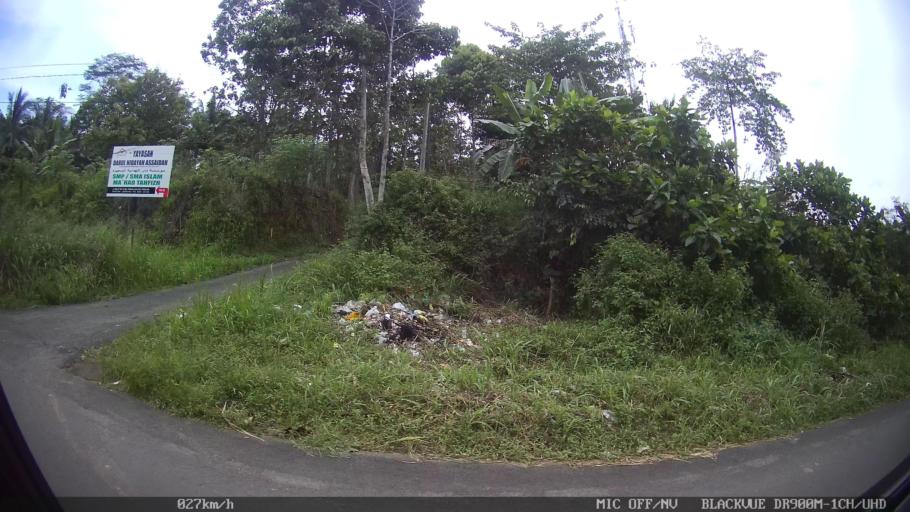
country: ID
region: Lampung
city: Kedaton
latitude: -5.3959
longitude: 105.1910
